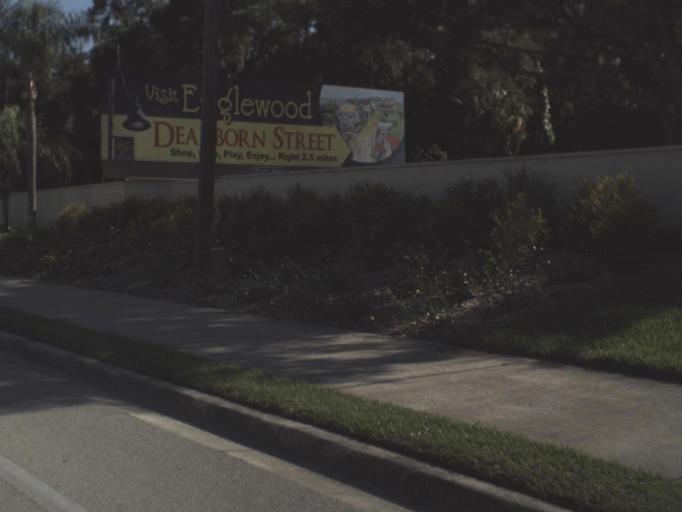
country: US
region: Florida
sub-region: Sarasota County
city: Englewood
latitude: 26.9924
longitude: -82.3699
